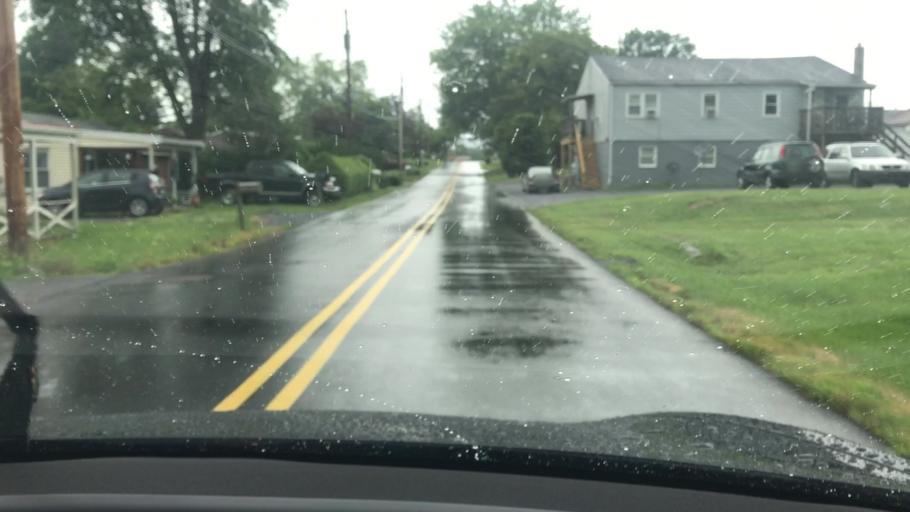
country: US
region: Pennsylvania
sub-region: Dauphin County
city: Paxtonia
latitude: 40.3140
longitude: -76.7949
